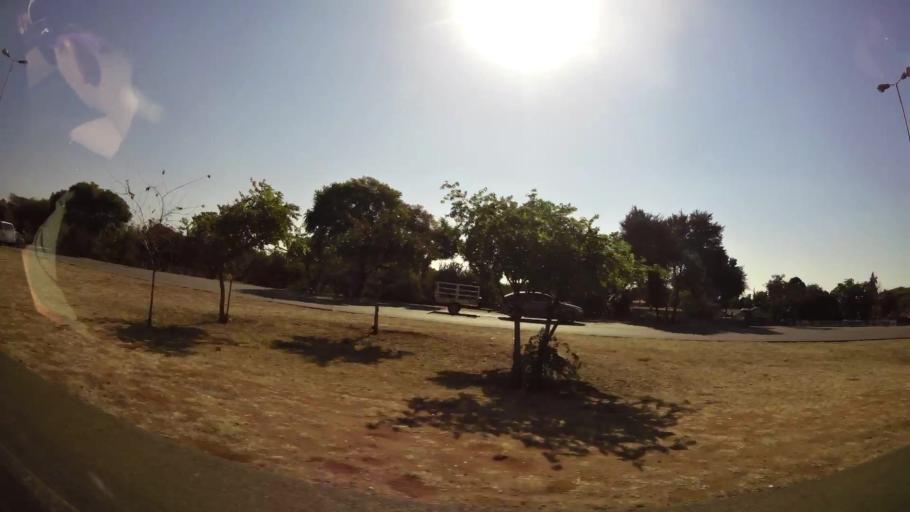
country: ZA
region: Gauteng
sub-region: City of Tshwane Metropolitan Municipality
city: Pretoria
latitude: -25.6805
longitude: 28.2345
